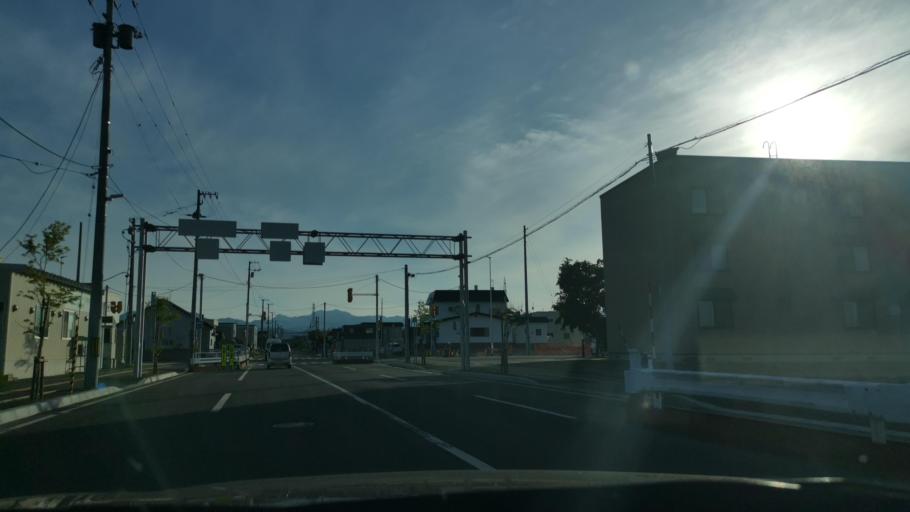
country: JP
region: Hokkaido
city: Sapporo
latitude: 43.0771
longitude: 141.4159
